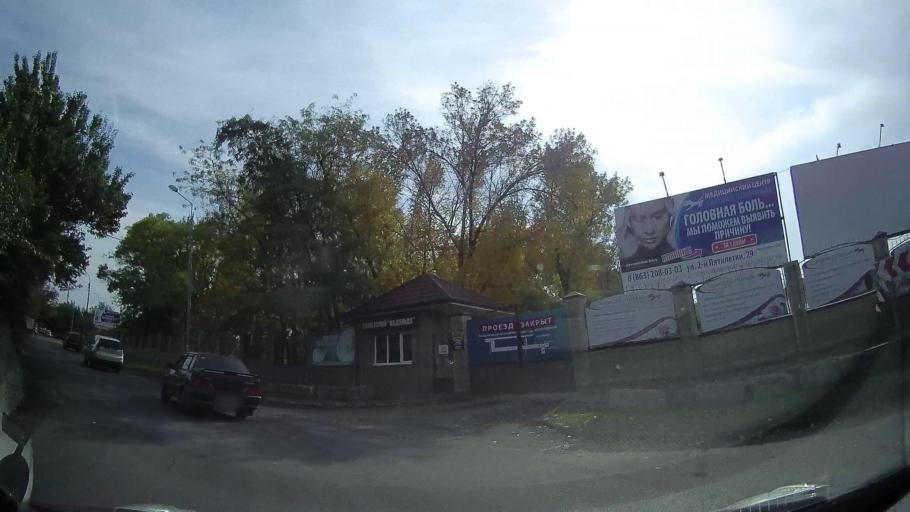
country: RU
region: Rostov
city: Severnyy
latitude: 47.2654
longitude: 39.7057
